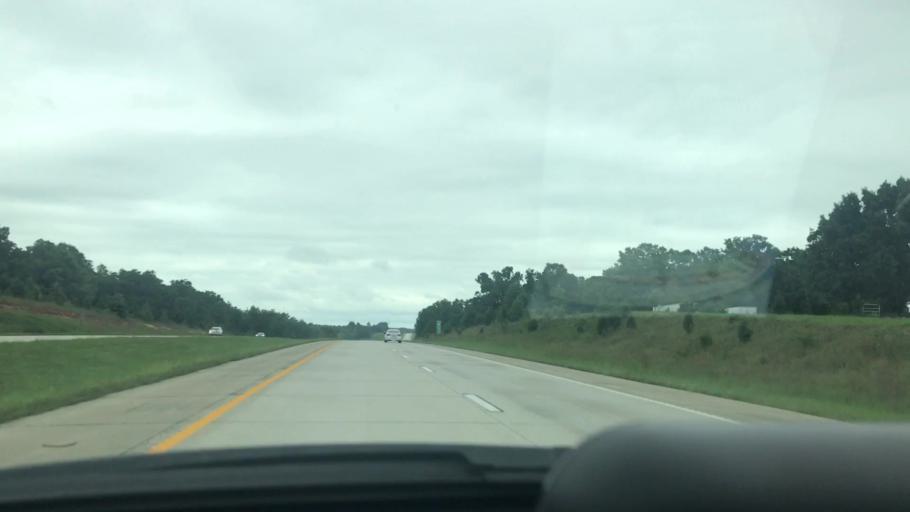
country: US
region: Missouri
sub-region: Dallas County
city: Buffalo
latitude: 37.5400
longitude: -93.1376
